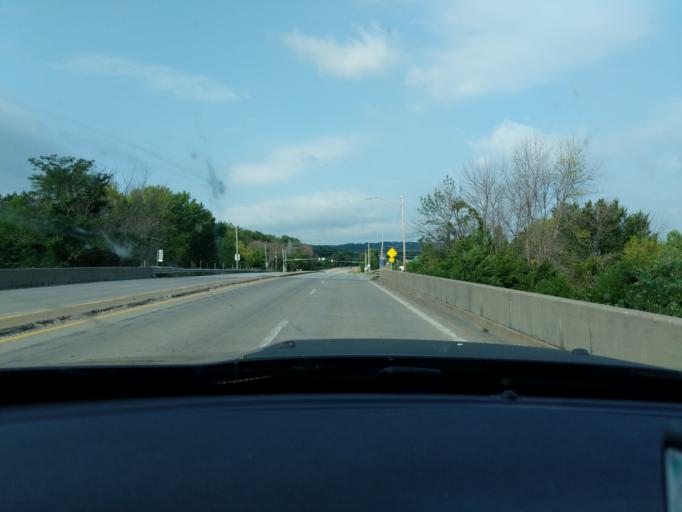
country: US
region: Illinois
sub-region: Rock Island County
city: Rock Island
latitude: 41.5018
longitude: -90.6212
